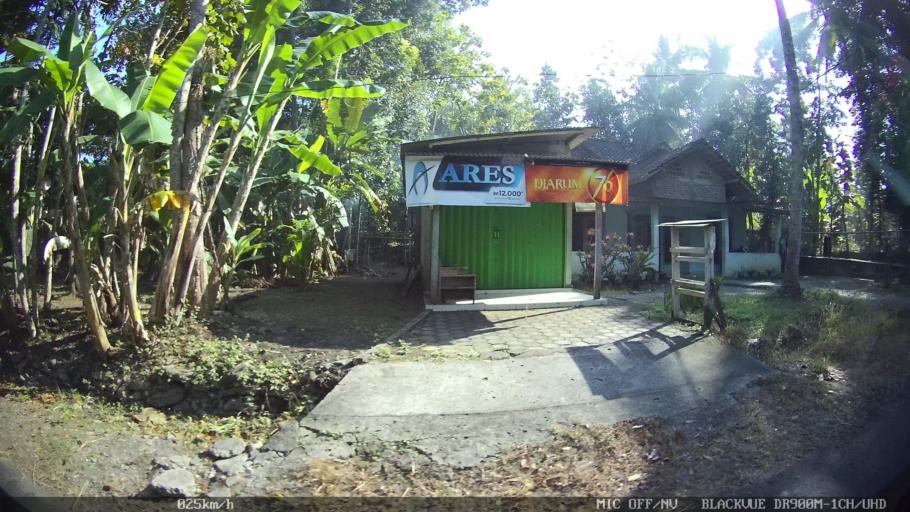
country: ID
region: Daerah Istimewa Yogyakarta
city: Kasihan
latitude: -7.8325
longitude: 110.2746
